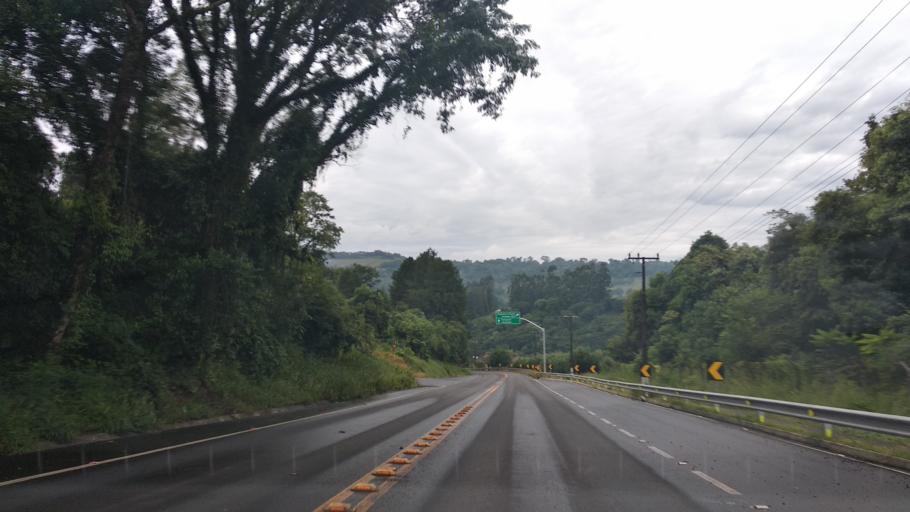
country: BR
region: Santa Catarina
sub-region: Videira
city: Videira
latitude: -27.0532
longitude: -51.2297
